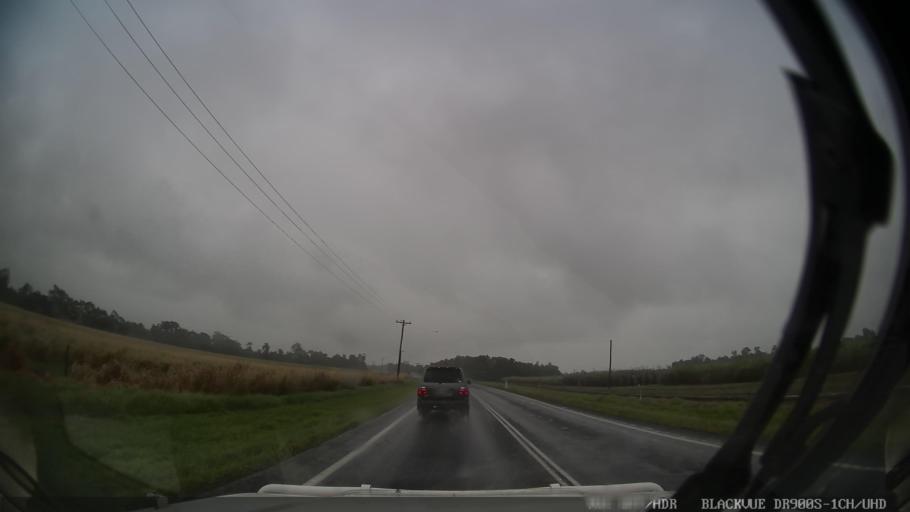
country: AU
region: Queensland
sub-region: Cassowary Coast
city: Innisfail
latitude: -17.6586
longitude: 146.0369
